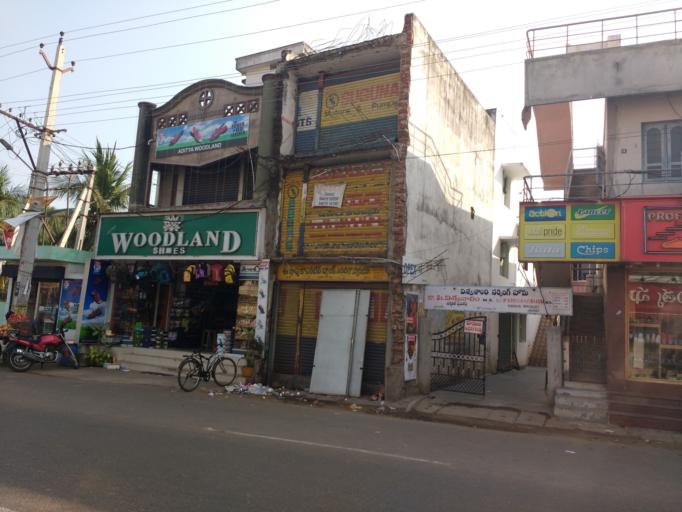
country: IN
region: Andhra Pradesh
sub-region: Srikakulam
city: Srikakulam
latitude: 18.2950
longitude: 83.8987
